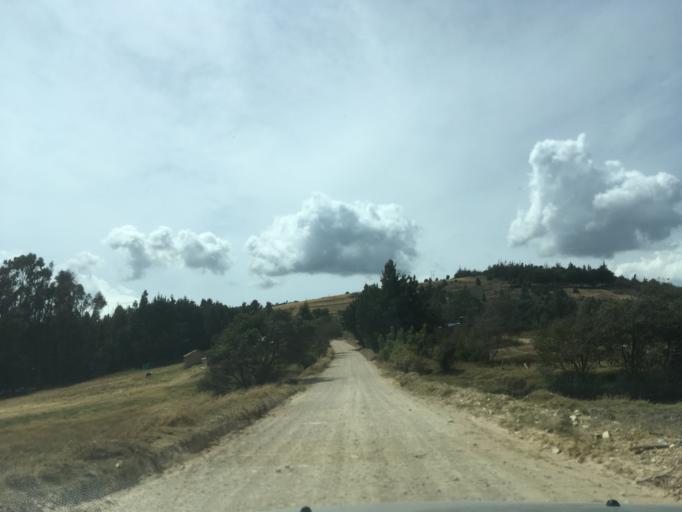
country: CO
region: Boyaca
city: Aquitania
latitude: 5.5629
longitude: -72.9514
